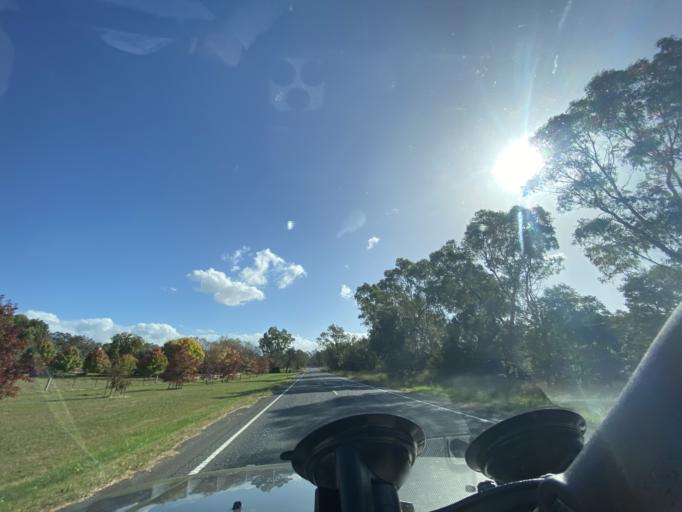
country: AU
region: Victoria
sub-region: Murrindindi
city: Kinglake West
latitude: -37.2473
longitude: 145.3809
